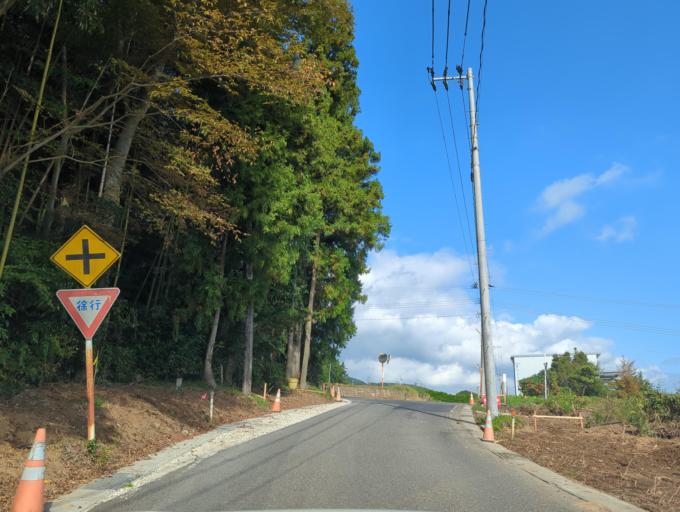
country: JP
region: Fukushima
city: Motomiya
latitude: 37.5532
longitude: 140.3444
